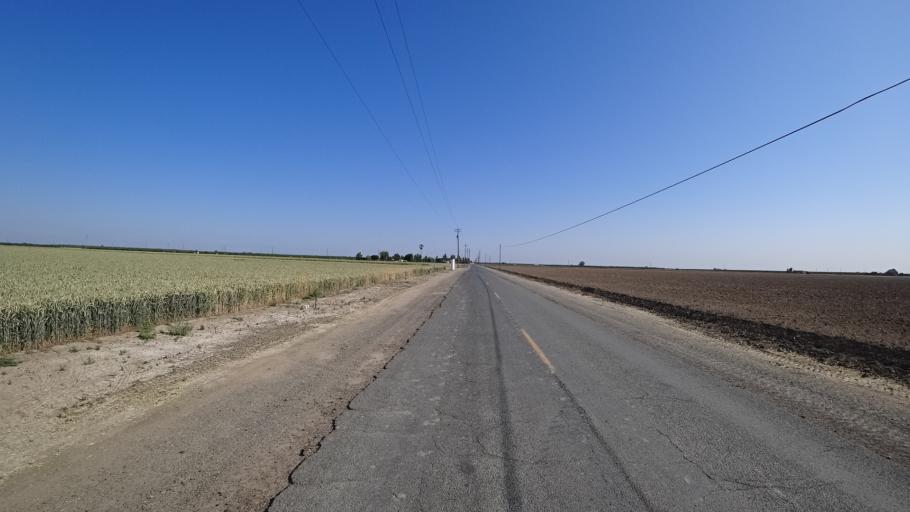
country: US
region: California
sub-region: Kings County
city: Home Garden
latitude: 36.2502
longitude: -119.5831
